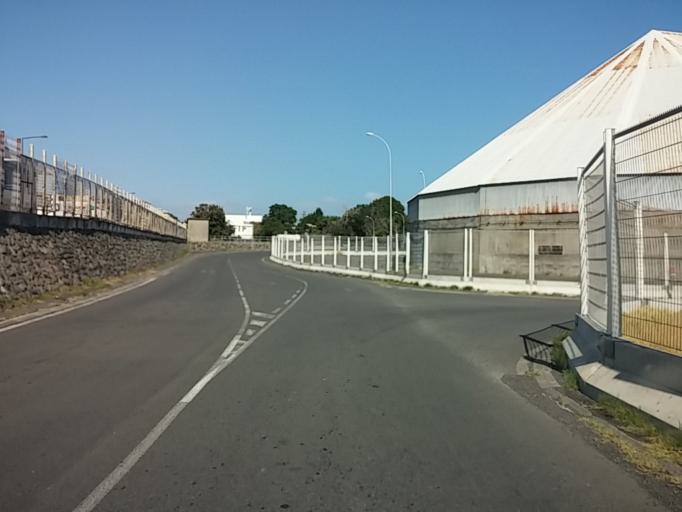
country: RE
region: Reunion
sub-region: Reunion
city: Le Port
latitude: -20.9356
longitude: 55.2896
